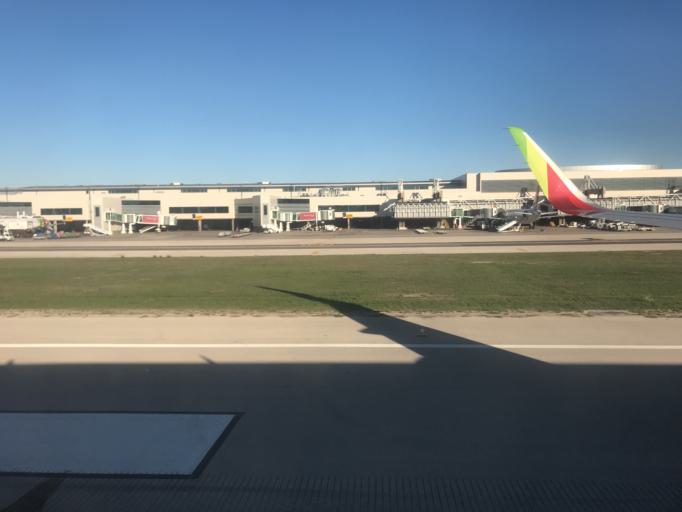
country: PT
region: Lisbon
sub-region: Loures
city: Moscavide
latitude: 38.7717
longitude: -9.1332
